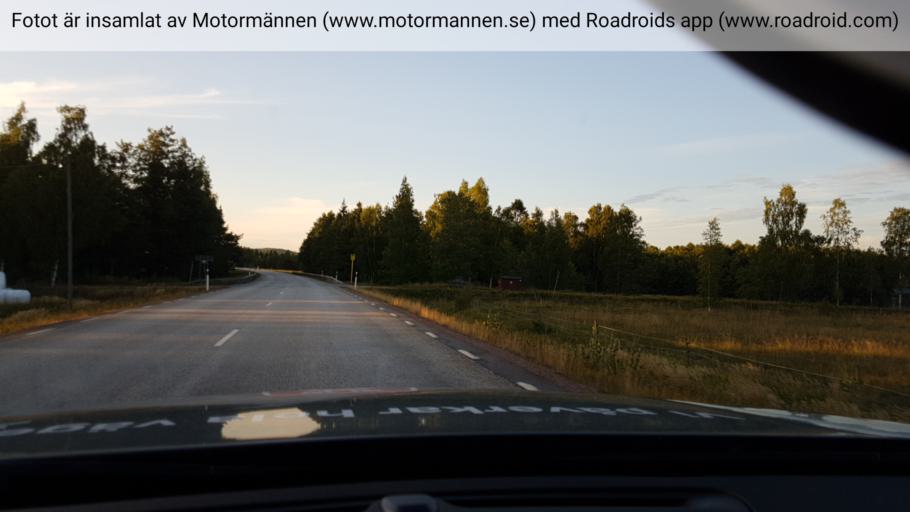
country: SE
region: Vaermland
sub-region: Storfors Kommun
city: Storfors
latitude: 59.4818
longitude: 14.3284
